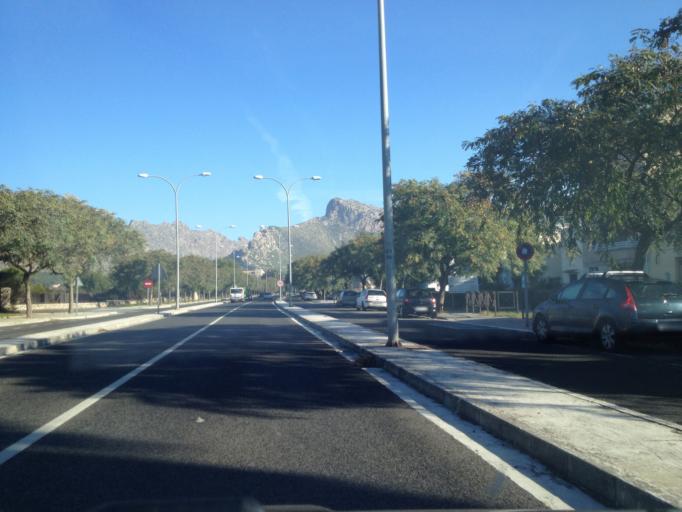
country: ES
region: Balearic Islands
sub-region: Illes Balears
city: Pollenca
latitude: 39.9059
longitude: 3.0762
